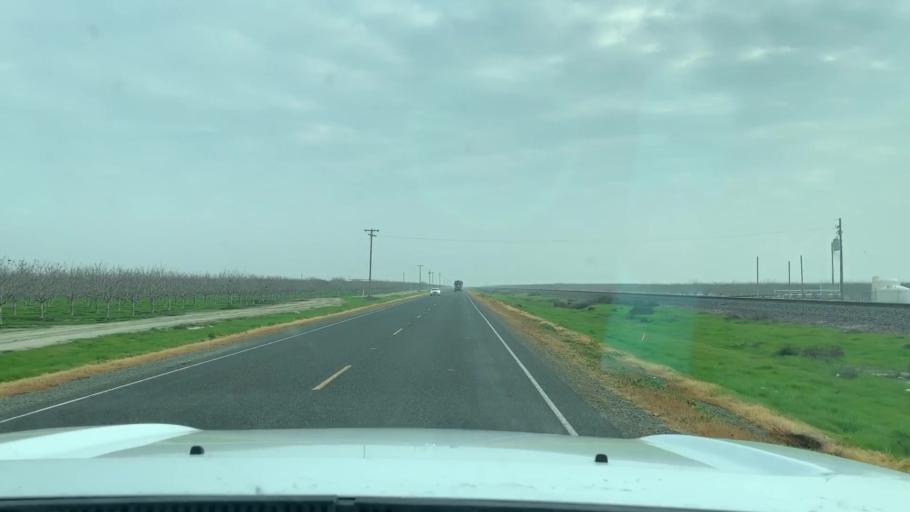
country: US
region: California
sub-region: Tulare County
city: Earlimart
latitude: 35.8298
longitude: -119.3689
